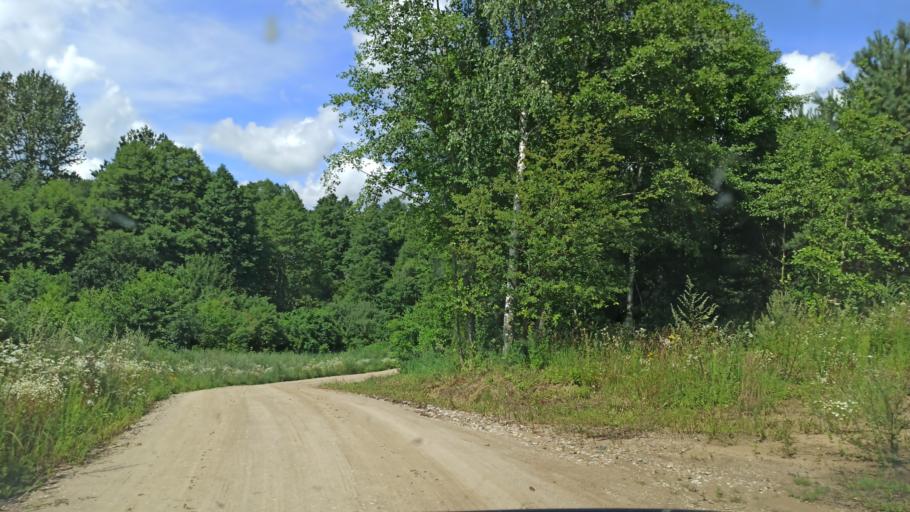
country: PL
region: Warmian-Masurian Voivodeship
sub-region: Powiat ostrodzki
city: Milakowo
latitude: 53.8564
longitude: 20.0668
